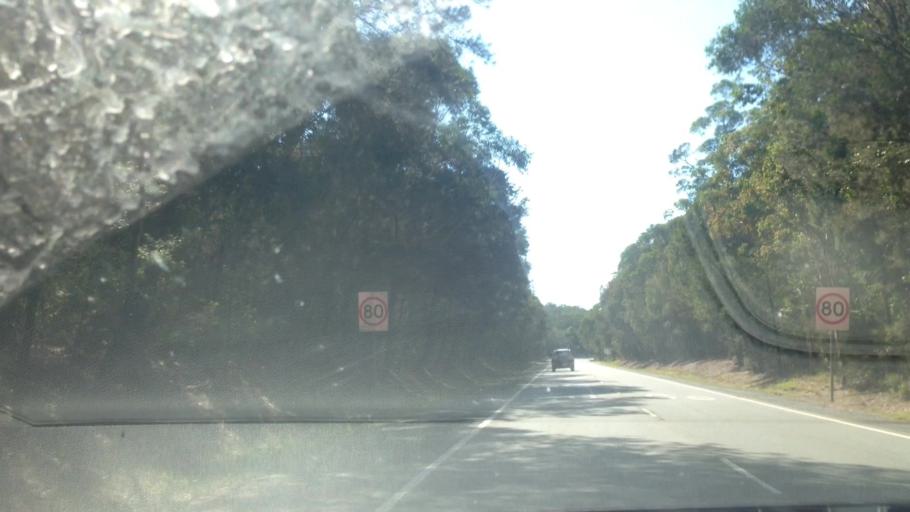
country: AU
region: New South Wales
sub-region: Lake Macquarie Shire
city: Toronto
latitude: -32.9867
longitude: 151.5118
